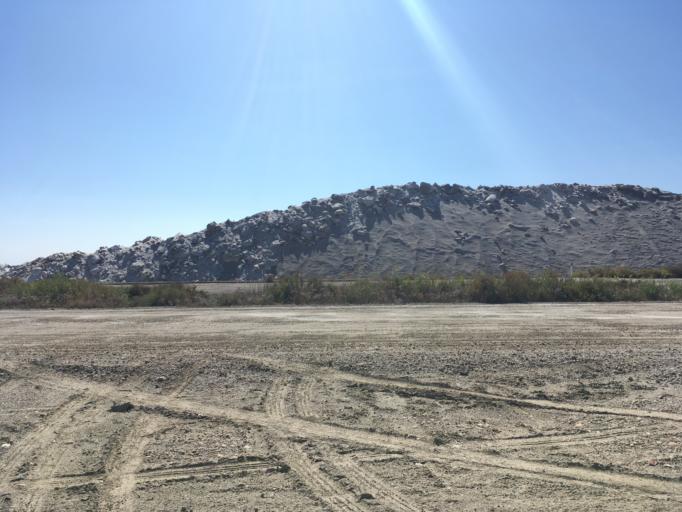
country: FR
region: Languedoc-Roussillon
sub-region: Departement du Gard
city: Aigues-Mortes
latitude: 43.5511
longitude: 4.1865
